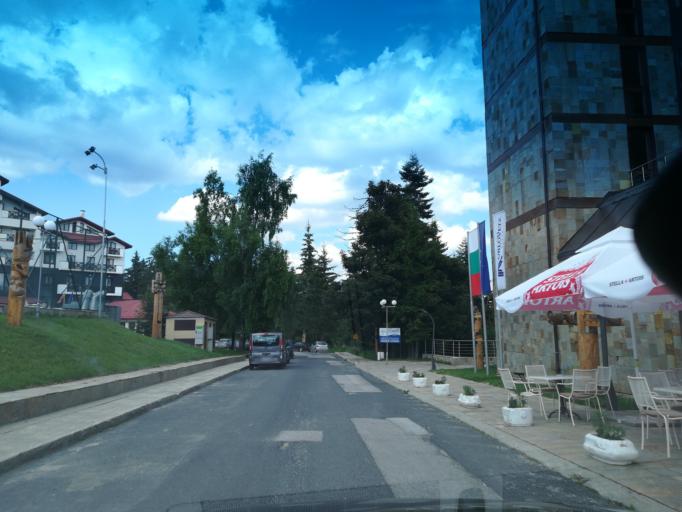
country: BG
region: Smolyan
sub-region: Obshtina Smolyan
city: Smolyan
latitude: 41.6585
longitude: 24.6991
